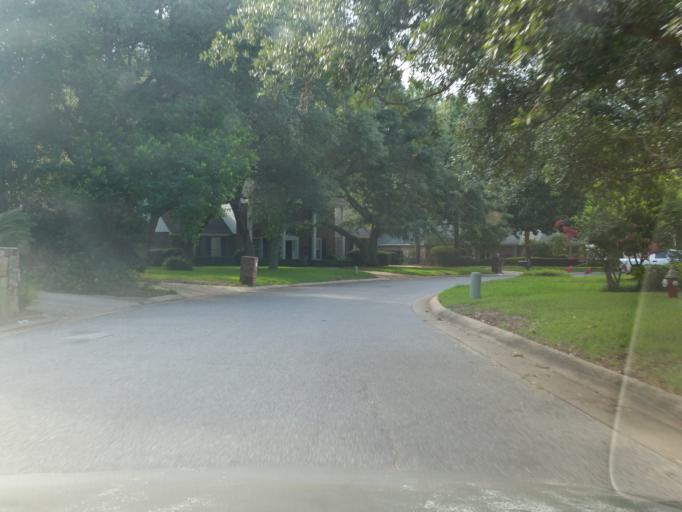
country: US
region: Florida
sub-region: Escambia County
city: Ferry Pass
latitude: 30.5016
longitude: -87.1657
